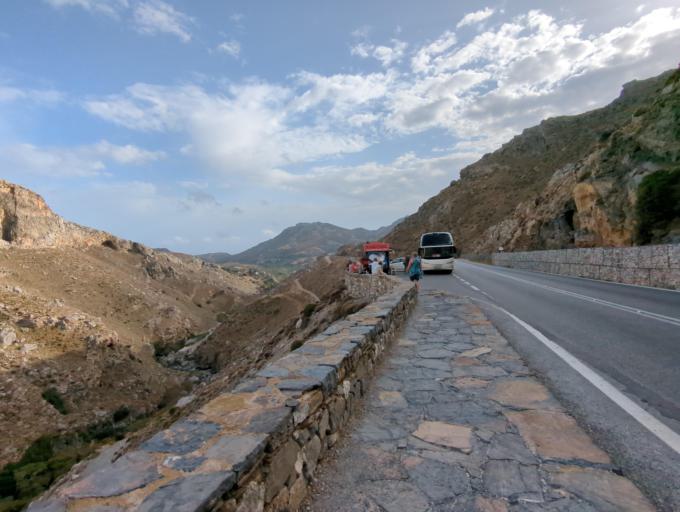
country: GR
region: Crete
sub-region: Nomos Rethymnis
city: Atsipopoulon
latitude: 35.1946
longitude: 24.4640
